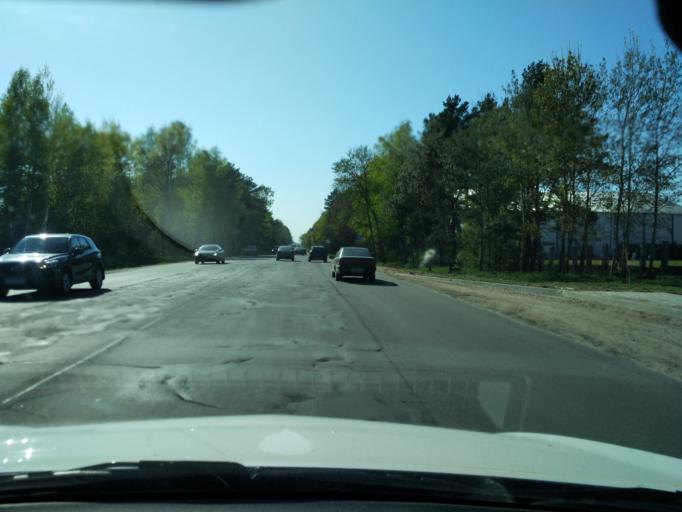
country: BY
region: Minsk
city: Borovlyany
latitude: 53.9653
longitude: 27.6637
